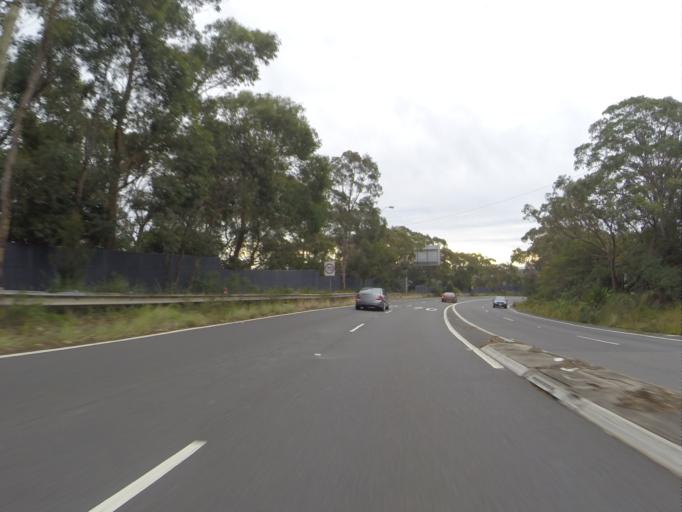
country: AU
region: New South Wales
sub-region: Sutherland Shire
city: Heathcote
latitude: -34.0761
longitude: 151.0072
